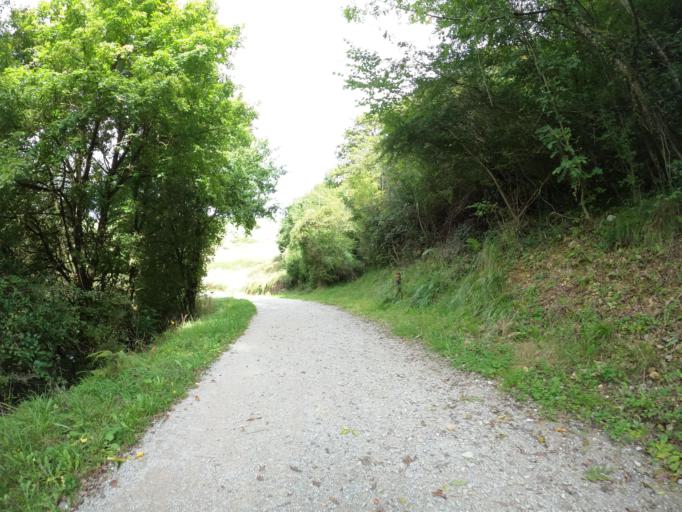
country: ES
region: Navarre
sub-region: Provincia de Navarra
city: Lekunberri
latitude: 42.9910
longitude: -1.8877
